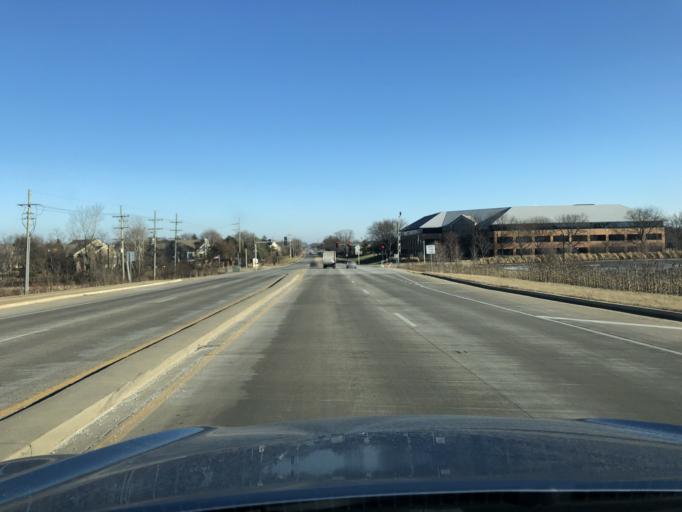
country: US
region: Illinois
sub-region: DuPage County
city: Itasca
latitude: 41.9924
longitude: -88.0223
